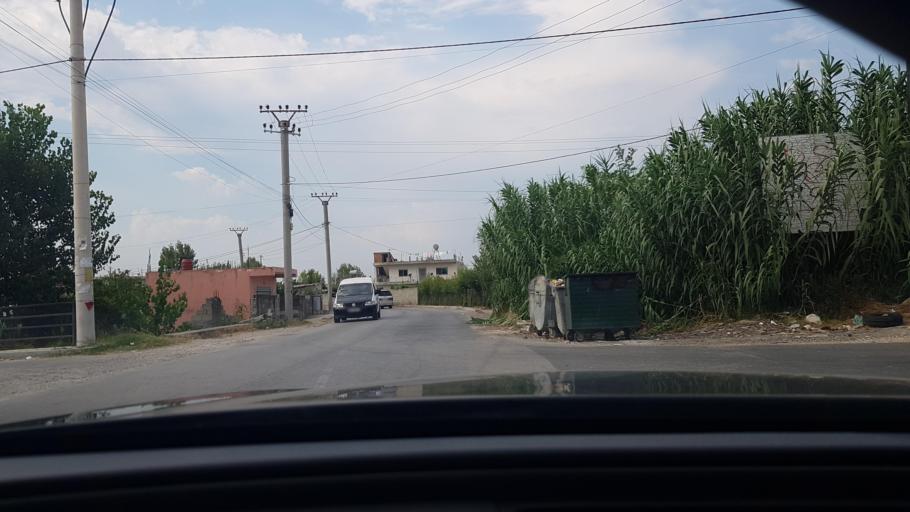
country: AL
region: Durres
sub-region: Rrethi i Durresit
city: Katundi i Ri
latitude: 41.4263
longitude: 19.5478
